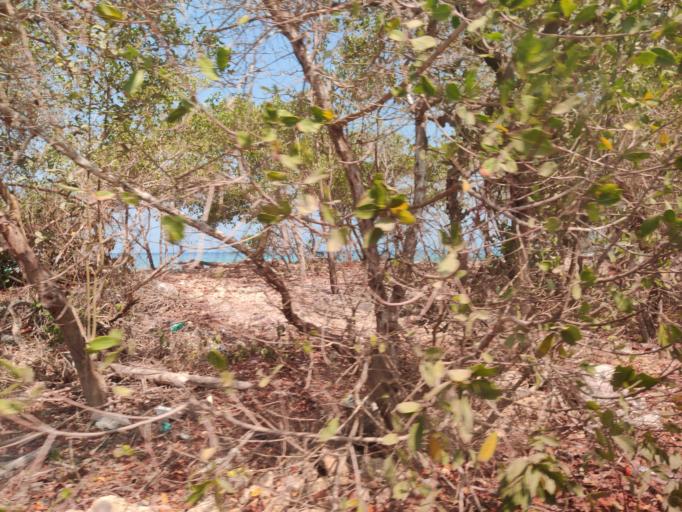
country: CO
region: Bolivar
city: Turbana
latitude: 10.1859
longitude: -75.6409
